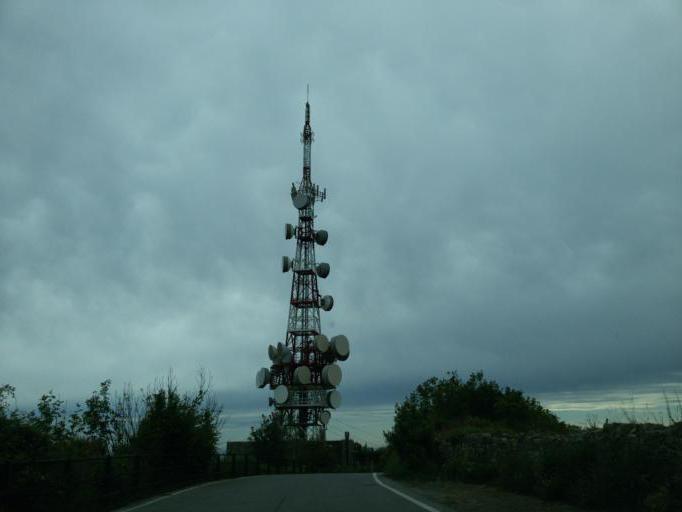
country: IT
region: Liguria
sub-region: Provincia di Genova
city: Genoa
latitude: 44.4314
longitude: 8.9130
